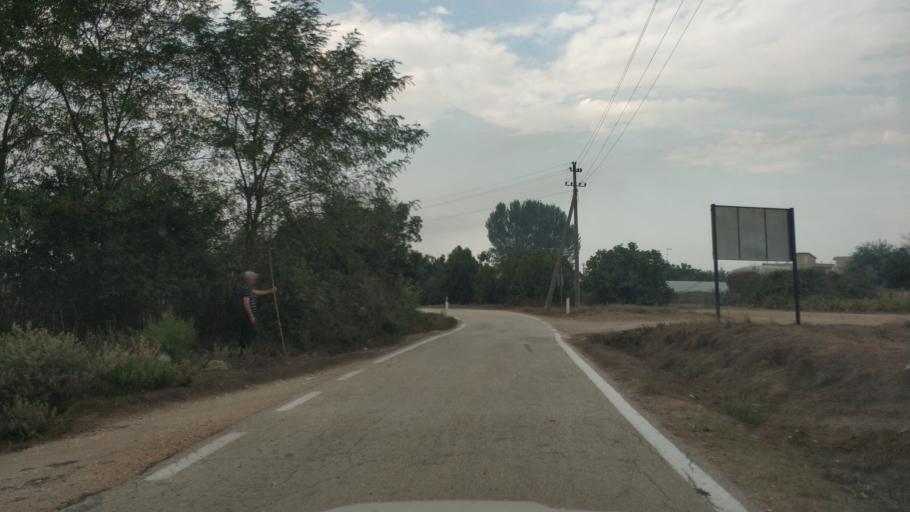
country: AL
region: Fier
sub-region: Rrethi i Fierit
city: Dermenas
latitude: 40.7257
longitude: 19.4684
